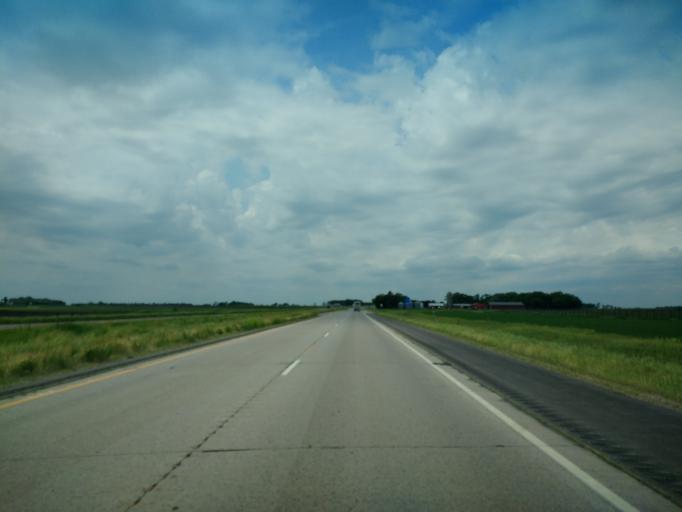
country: US
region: Minnesota
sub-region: Cottonwood County
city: Mountain Lake
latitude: 43.9491
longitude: -94.8149
